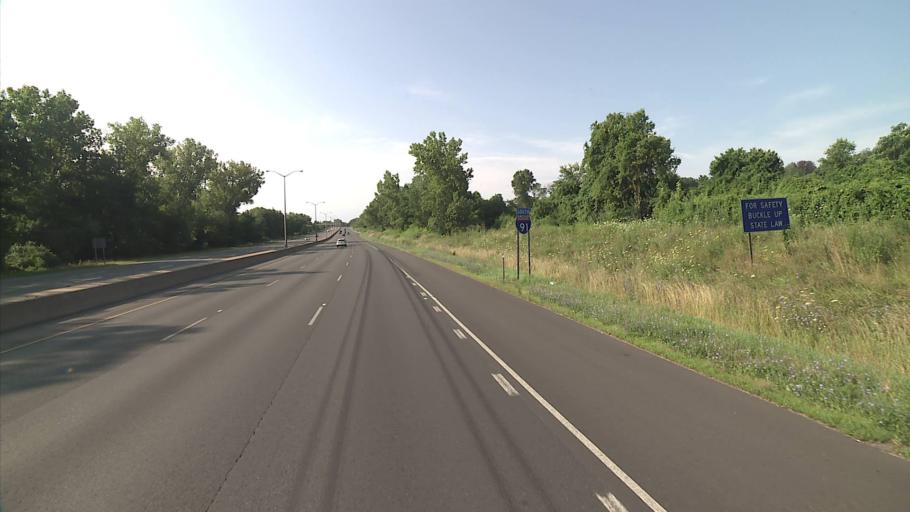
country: US
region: Connecticut
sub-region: Hartford County
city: Enfield
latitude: 41.9845
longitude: -72.5887
